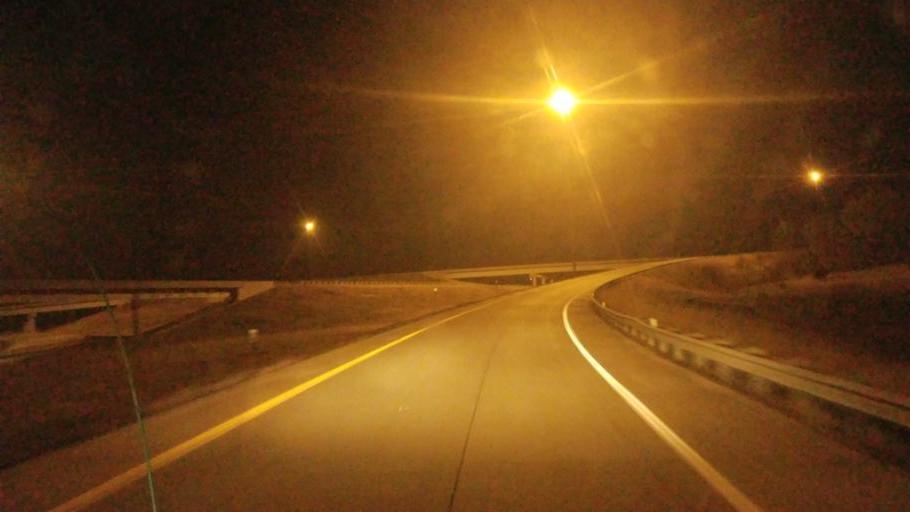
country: US
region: Missouri
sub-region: Howell County
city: Willow Springs
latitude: 36.9628
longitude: -91.9308
